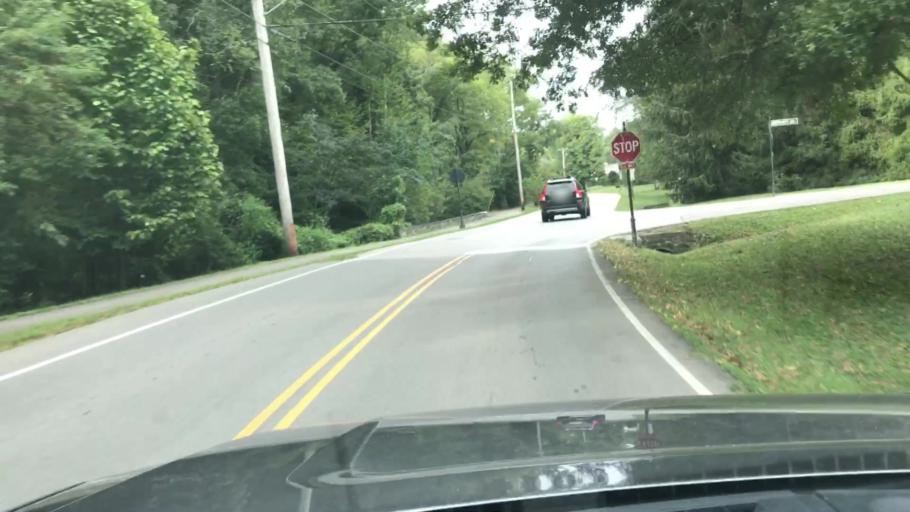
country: US
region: Tennessee
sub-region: Davidson County
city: Forest Hills
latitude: 36.0639
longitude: -86.8260
